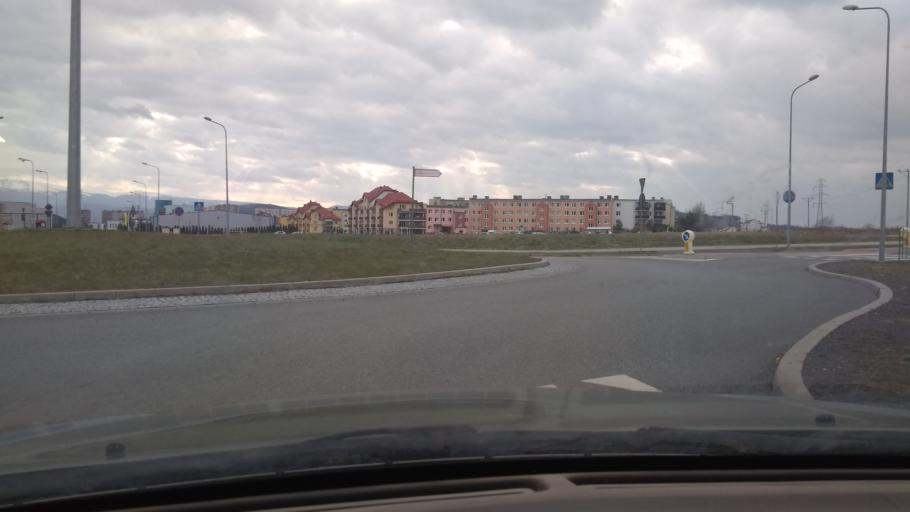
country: PL
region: Lower Silesian Voivodeship
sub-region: Powiat jeleniogorski
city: Jezow Sudecki
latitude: 50.9238
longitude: 15.7639
